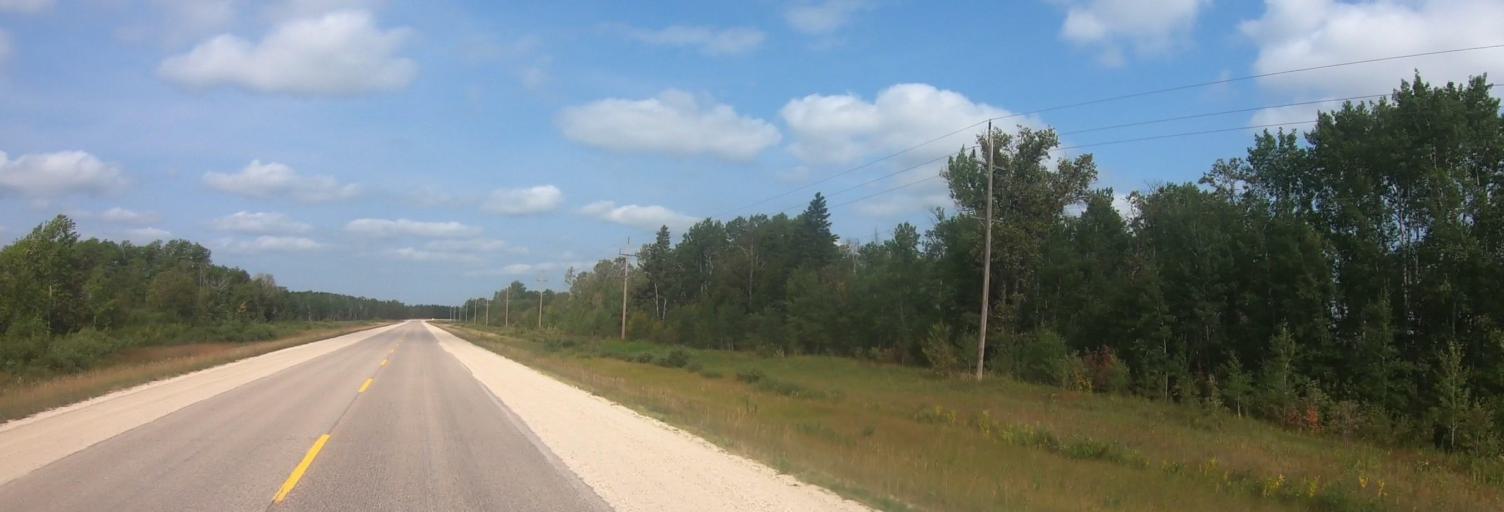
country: CA
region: Manitoba
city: La Broquerie
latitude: 49.2336
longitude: -96.3364
